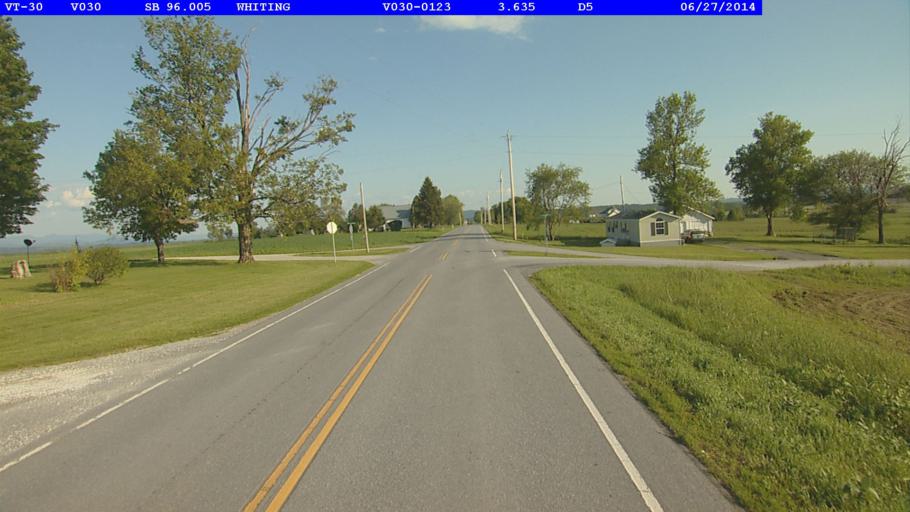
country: US
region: Vermont
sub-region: Addison County
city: Middlebury (village)
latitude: 43.8897
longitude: -73.2019
